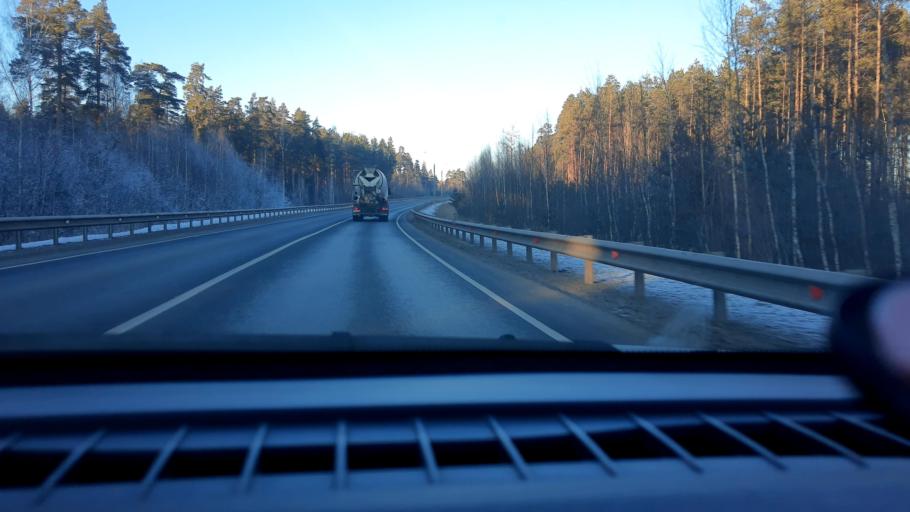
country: RU
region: Nizjnij Novgorod
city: Kstovo
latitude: 56.1699
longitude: 44.1534
